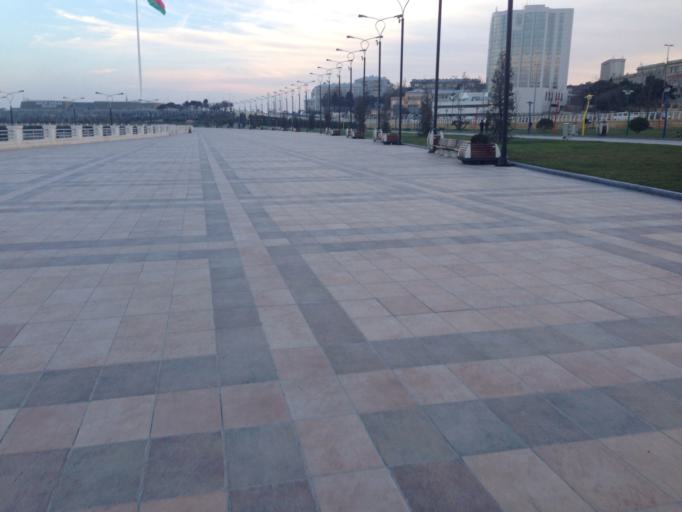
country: AZ
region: Baki
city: Badamdar
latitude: 40.3495
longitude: 49.8377
